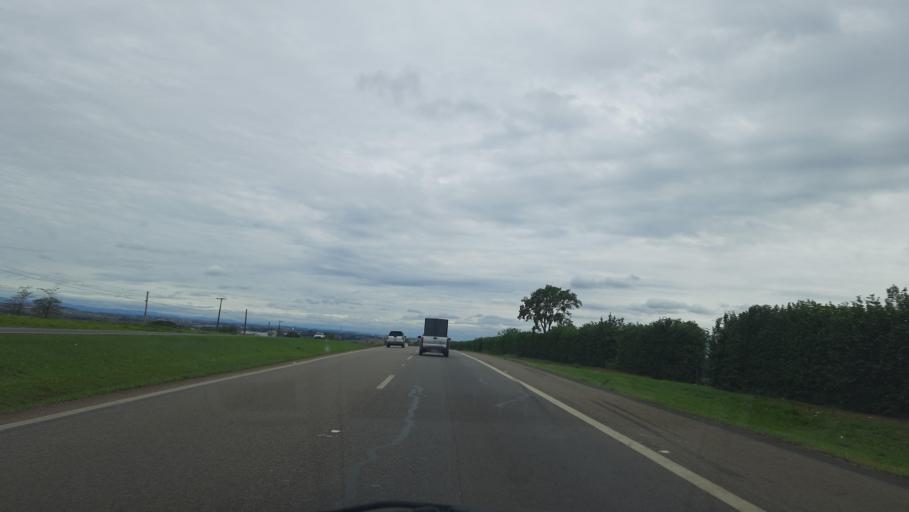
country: BR
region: Sao Paulo
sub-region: Moji-Guacu
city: Mogi-Gaucu
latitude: -22.2554
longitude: -46.9774
